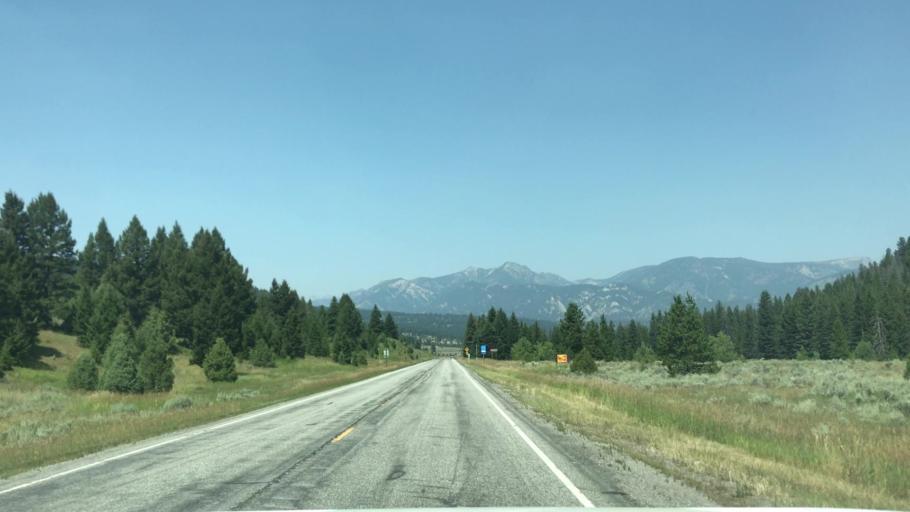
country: US
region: Montana
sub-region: Gallatin County
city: Big Sky
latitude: 45.2075
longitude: -111.2441
